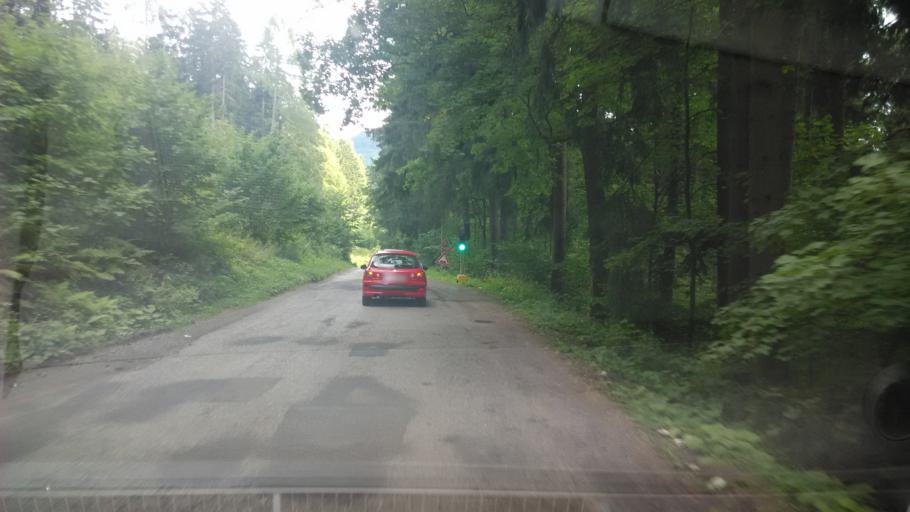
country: SK
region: Banskobystricky
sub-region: Okres Ziar nad Hronom
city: Kremnica
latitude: 48.7178
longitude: 18.9494
